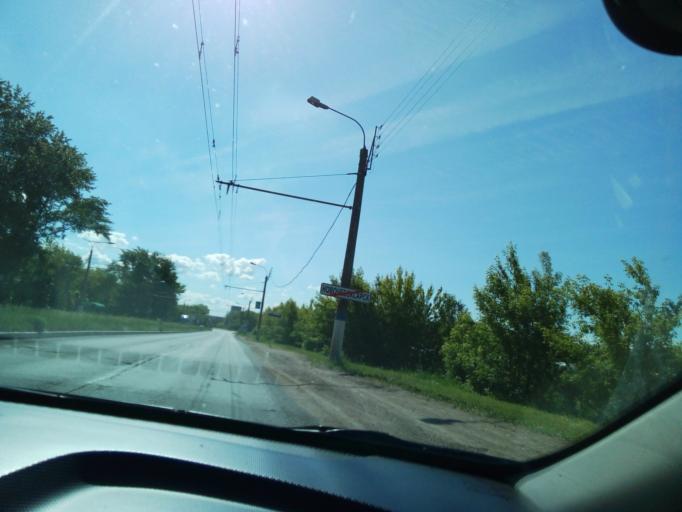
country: RU
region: Chuvashia
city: Novocheboksarsk
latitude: 56.0924
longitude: 47.4985
